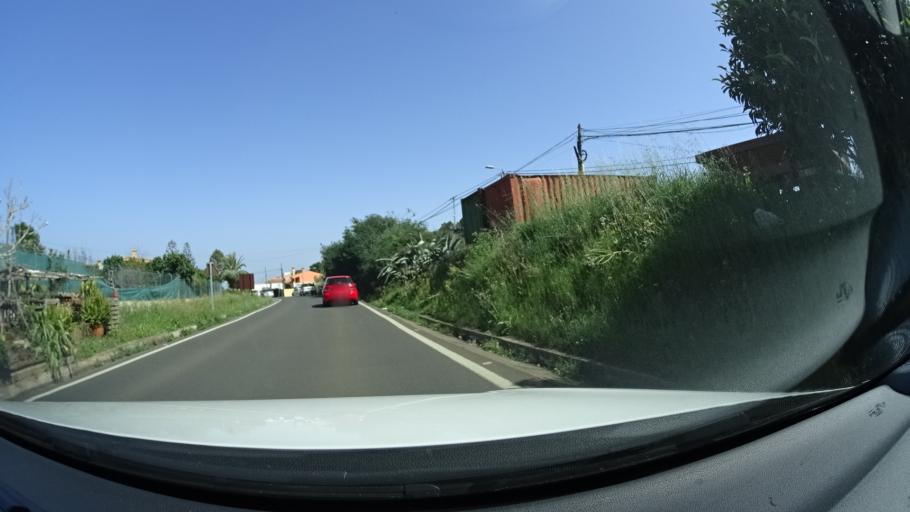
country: ES
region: Canary Islands
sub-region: Provincia de Las Palmas
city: Teror
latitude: 28.0863
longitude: -15.5373
